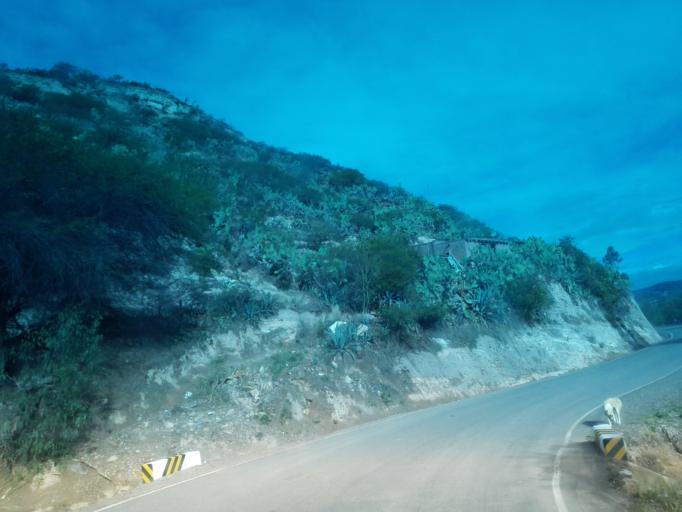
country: PE
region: Ayacucho
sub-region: Provincia de Huamanga
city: Pacaycasa
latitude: -13.0746
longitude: -74.2443
